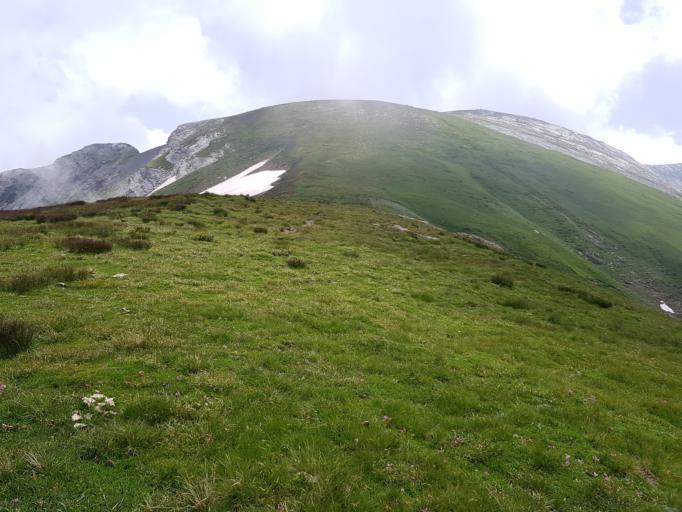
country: IT
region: Piedmont
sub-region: Provincia di Cuneo
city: Frabosa Soprana
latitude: 44.1889
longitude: 7.7732
